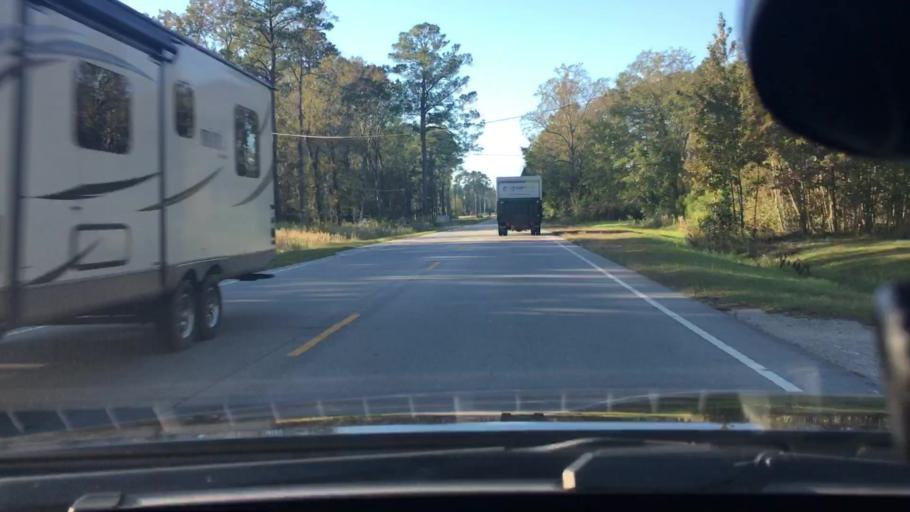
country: US
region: North Carolina
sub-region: Craven County
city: Vanceboro
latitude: 35.2539
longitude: -77.0935
